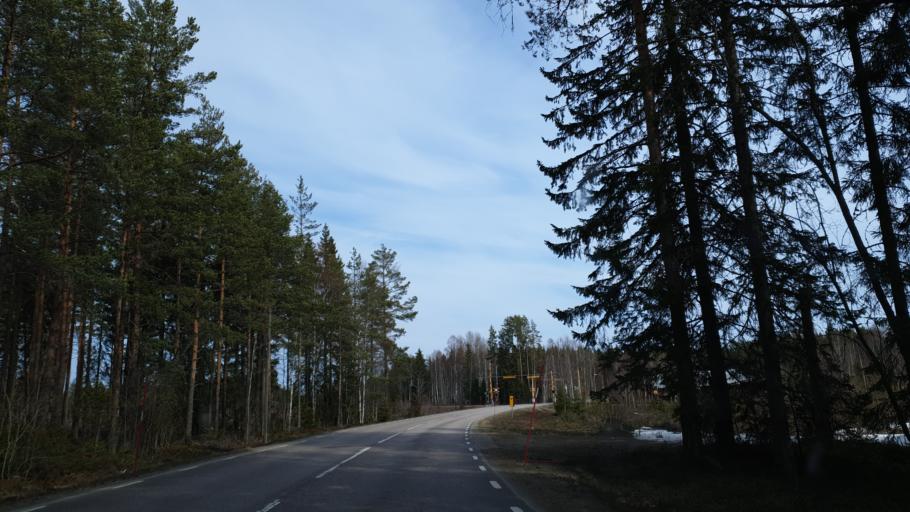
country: SE
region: Gaevleborg
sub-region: Gavle Kommun
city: Norrsundet
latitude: 60.9981
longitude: 17.0928
